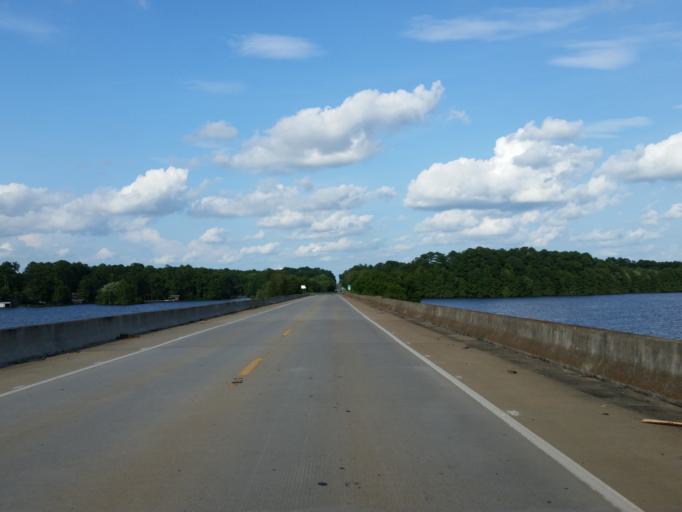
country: US
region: Georgia
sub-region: Crisp County
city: Cordele
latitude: 31.9652
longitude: -83.9310
